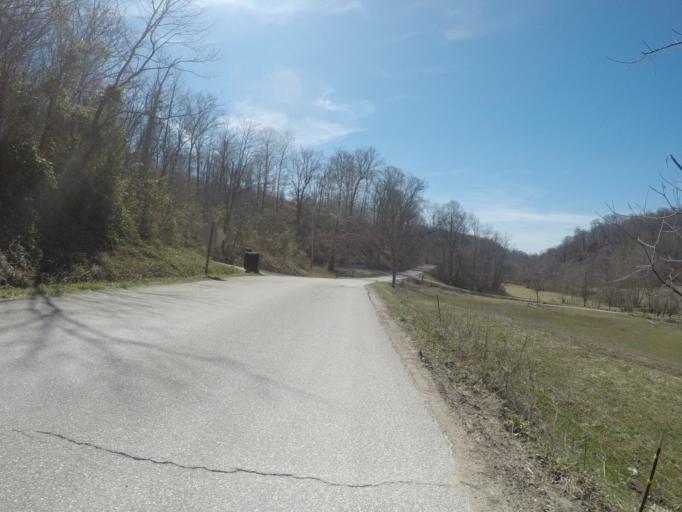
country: US
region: Ohio
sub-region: Lawrence County
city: South Point
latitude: 38.4697
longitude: -82.5675
